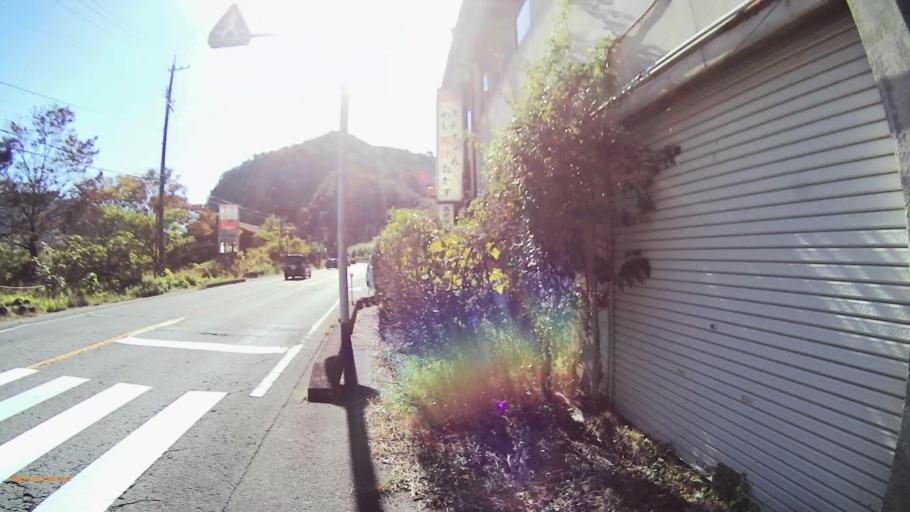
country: JP
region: Gifu
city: Inuyama
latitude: 35.4170
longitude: 136.9598
